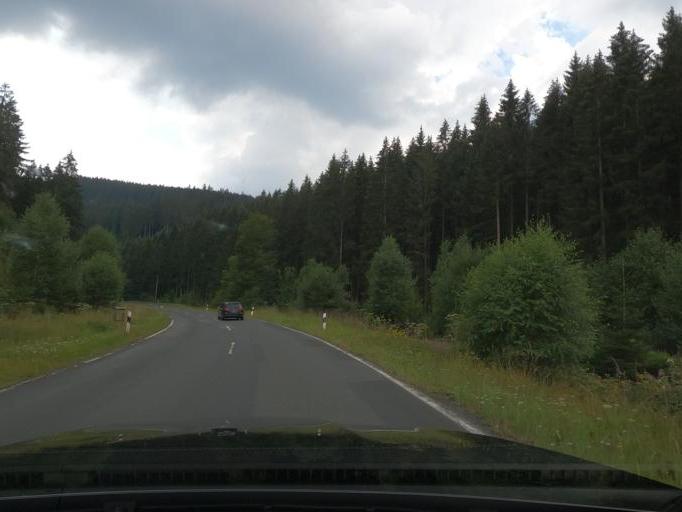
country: DE
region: Lower Saxony
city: Wildemann
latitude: 51.8406
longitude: 10.2633
